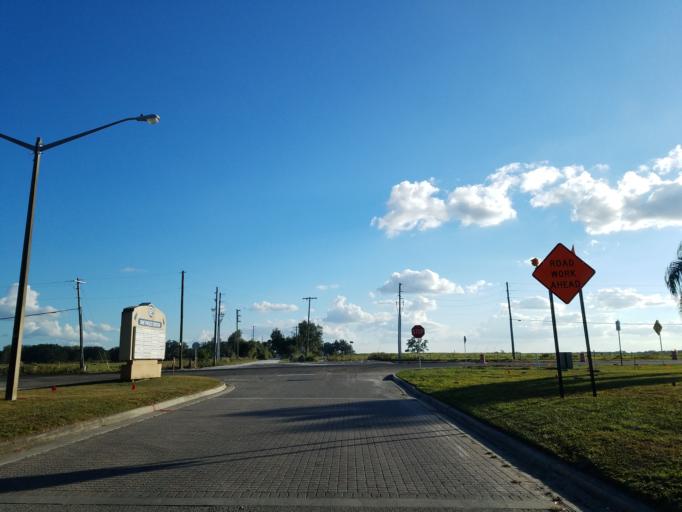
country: US
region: Florida
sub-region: Pasco County
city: San Antonio
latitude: 28.3257
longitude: -82.3124
